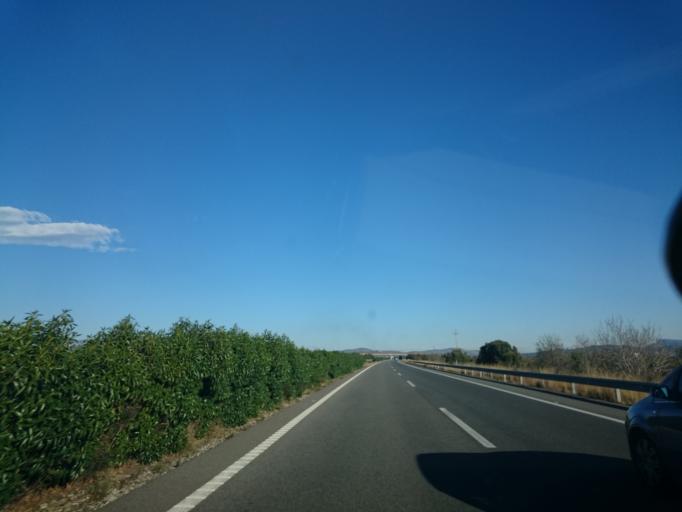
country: ES
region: Catalonia
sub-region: Provincia de Tarragona
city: Alcanar
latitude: 40.5207
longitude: 0.4162
